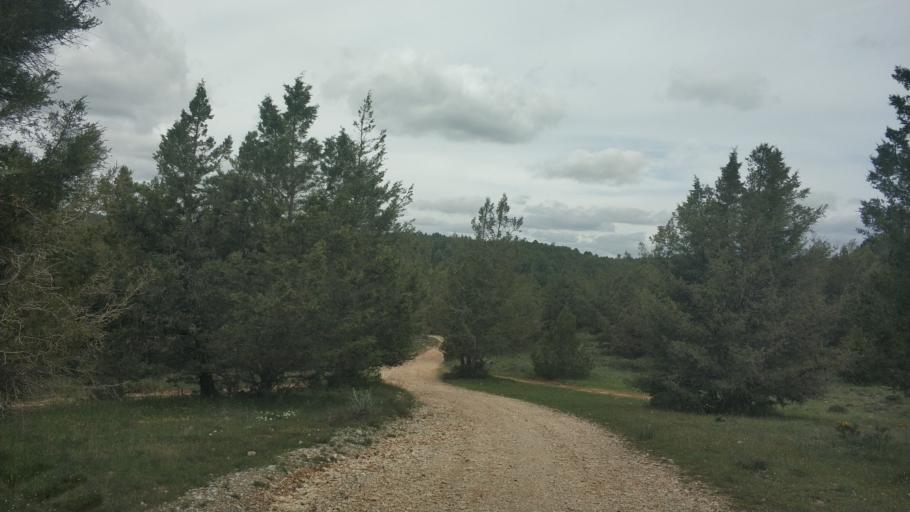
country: ES
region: Castille and Leon
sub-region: Provincia de Soria
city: Herrera de Soria
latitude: 41.7705
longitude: -3.0317
